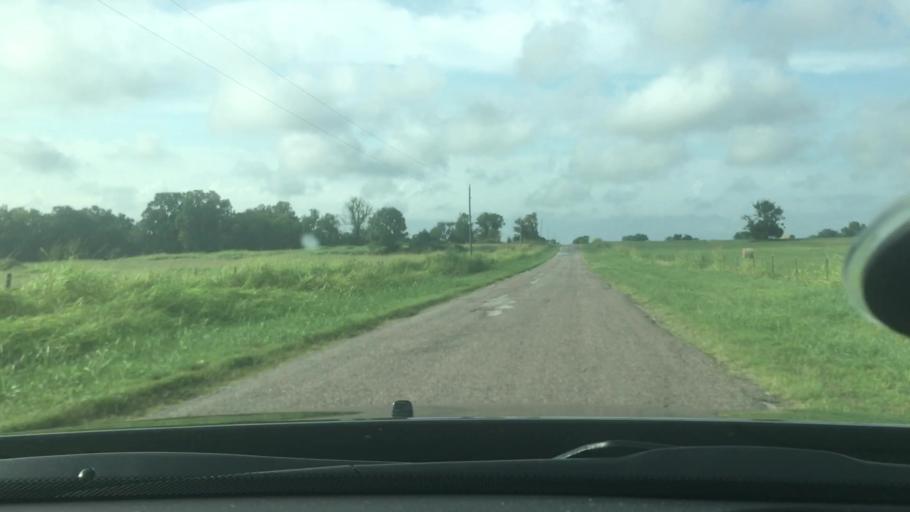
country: US
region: Oklahoma
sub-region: Pontotoc County
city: Ada
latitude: 34.6863
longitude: -96.5298
